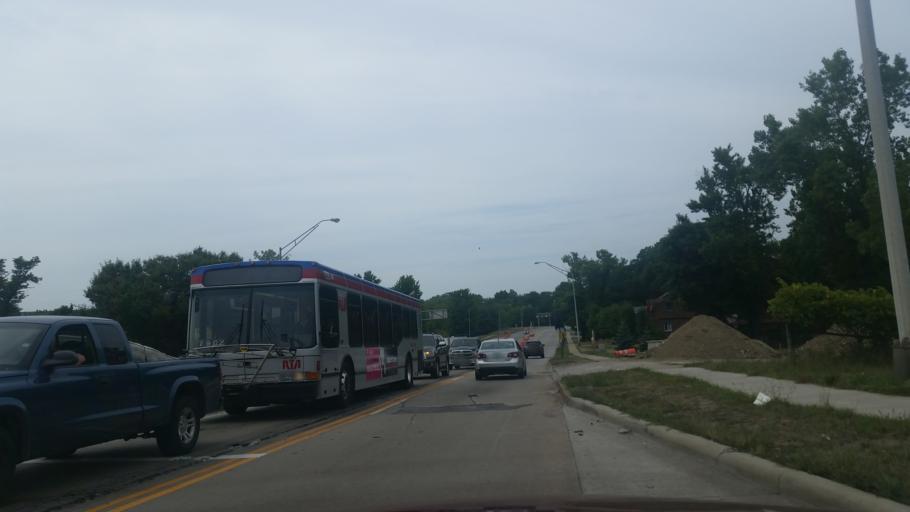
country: US
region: Ohio
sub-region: Cuyahoga County
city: Brooklyn
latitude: 41.4271
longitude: -81.7616
